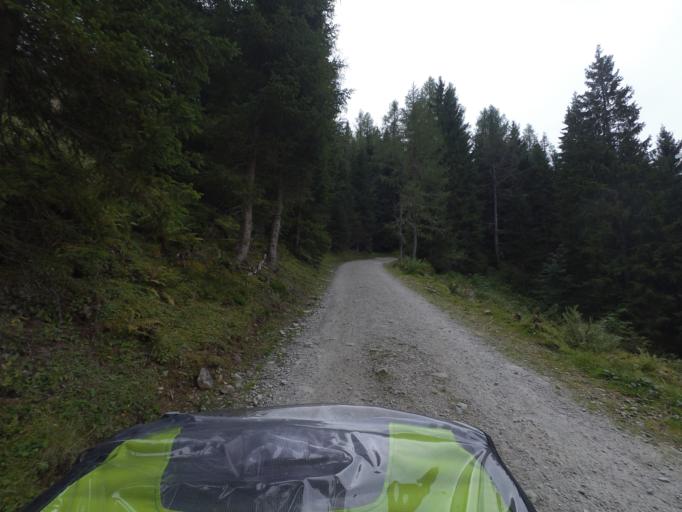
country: AT
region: Salzburg
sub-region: Politischer Bezirk Sankt Johann im Pongau
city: Untertauern
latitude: 47.2912
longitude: 13.5785
